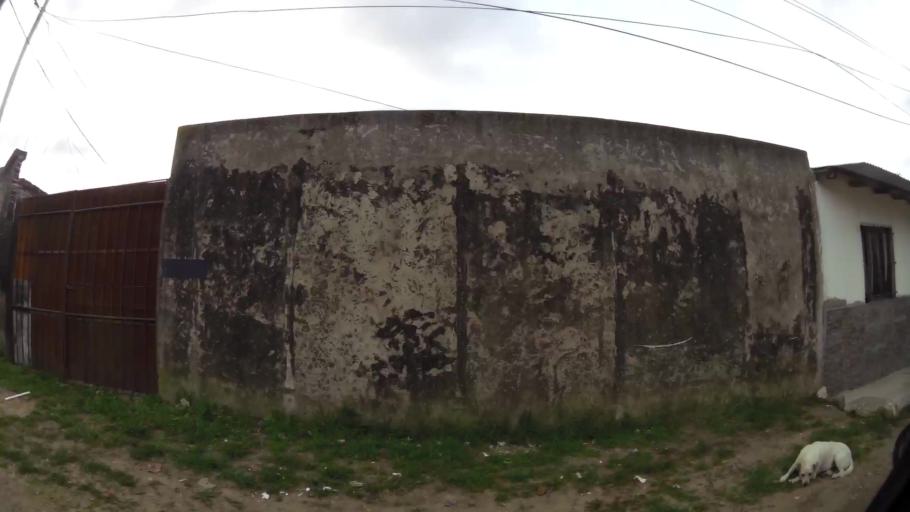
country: AR
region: Buenos Aires
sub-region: Partido de Quilmes
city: Quilmes
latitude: -34.7268
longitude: -58.2351
